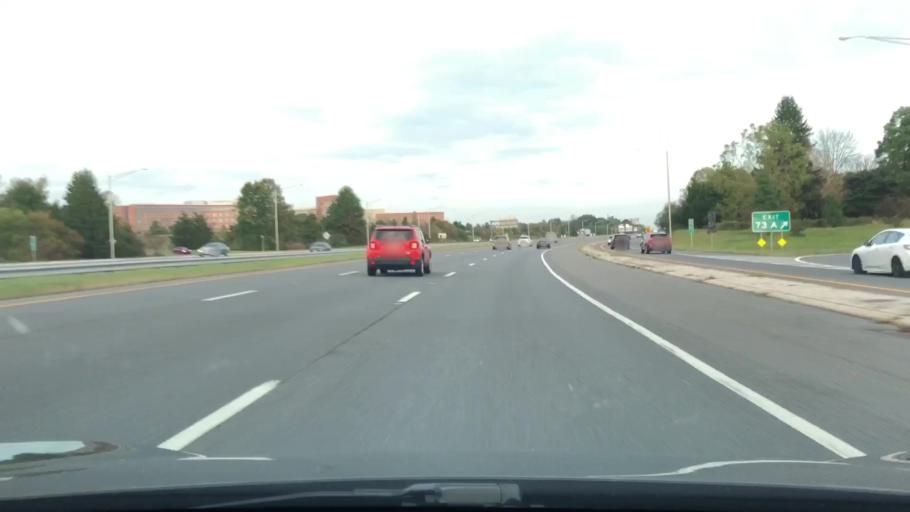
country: US
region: New Jersey
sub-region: Mercer County
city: Ewing
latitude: 40.2893
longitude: -74.8108
